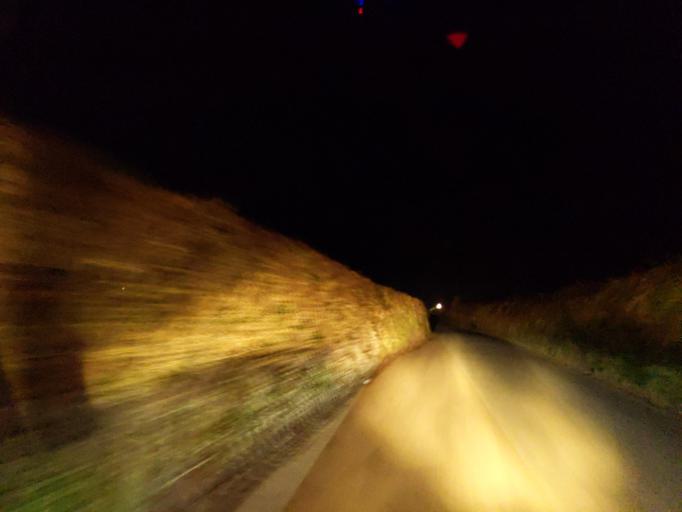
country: GB
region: England
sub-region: Cornwall
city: Torpoint
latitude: 50.3505
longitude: -4.2306
